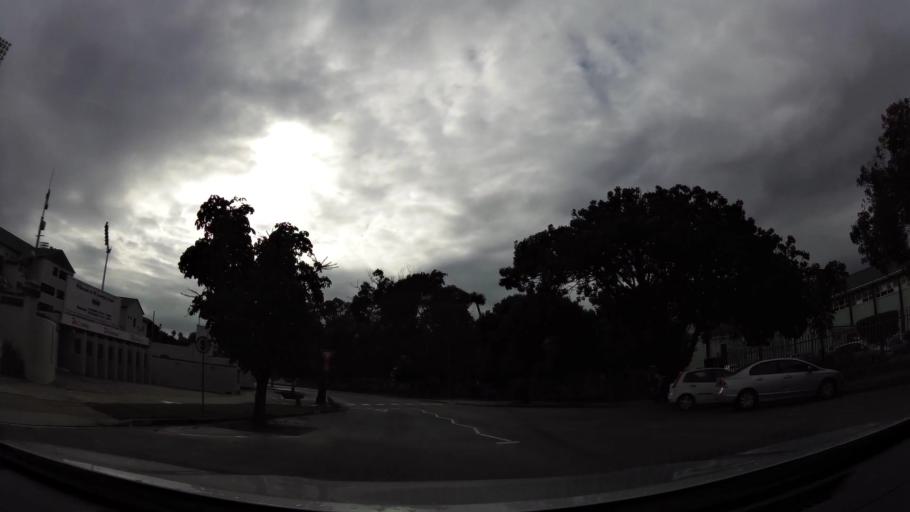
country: ZA
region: Eastern Cape
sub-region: Nelson Mandela Bay Metropolitan Municipality
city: Port Elizabeth
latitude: -33.9678
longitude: 25.6103
